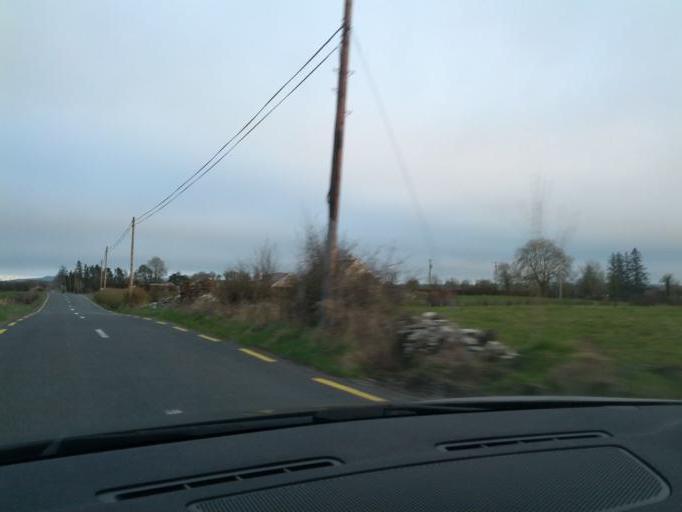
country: IE
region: Connaught
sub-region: Sligo
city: Ballymote
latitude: 54.0178
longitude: -8.5596
